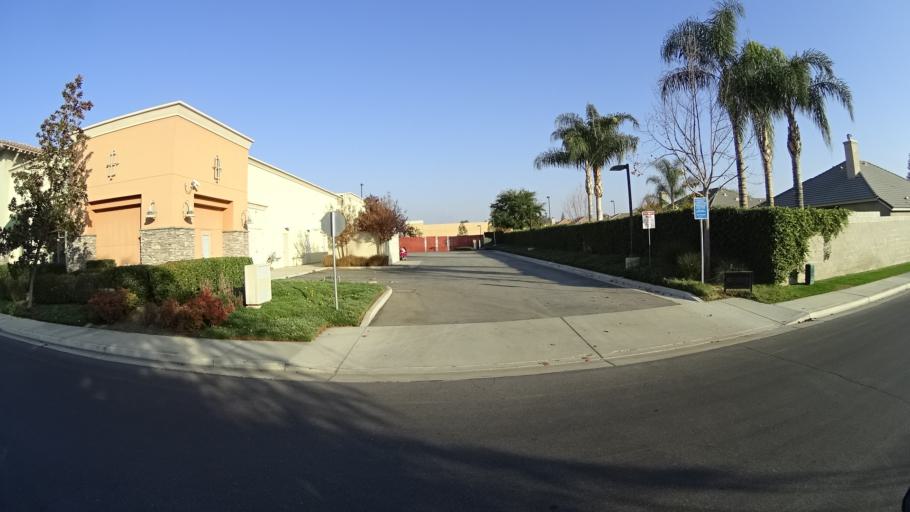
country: US
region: California
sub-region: Kern County
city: Rosedale
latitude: 35.3822
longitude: -119.1491
